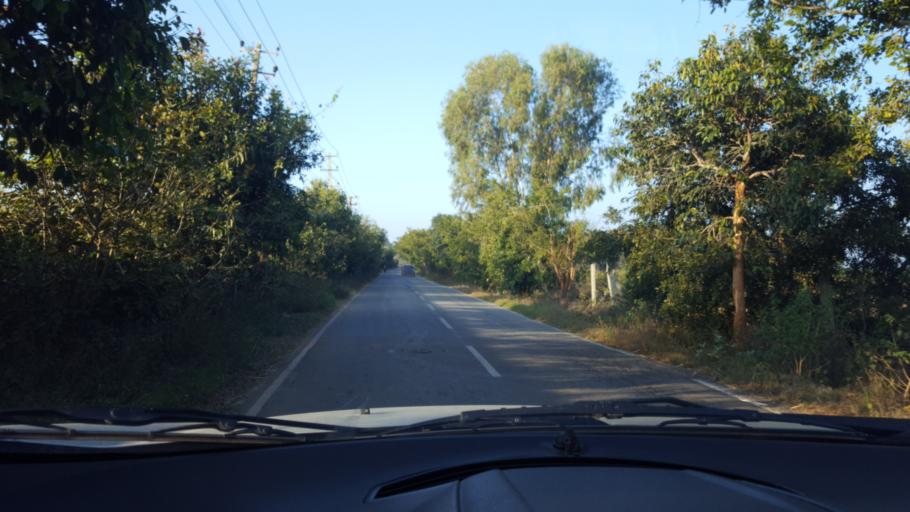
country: IN
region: Karnataka
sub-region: Bangalore Urban
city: Yelahanka
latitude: 13.1757
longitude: 77.5992
